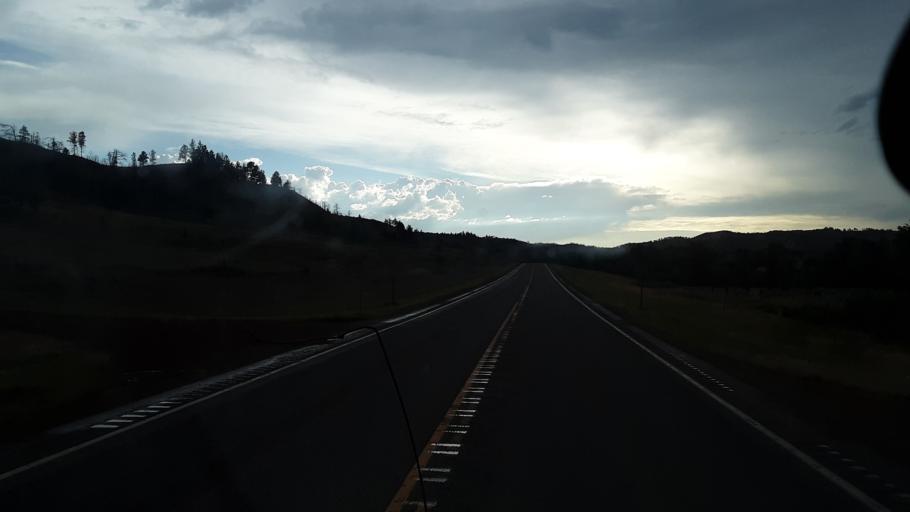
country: US
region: Montana
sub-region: Rosebud County
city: Lame Deer
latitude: 45.6184
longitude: -106.3985
